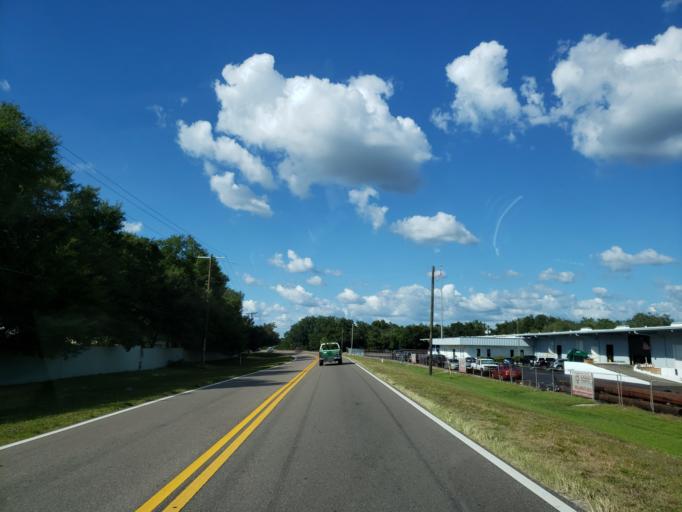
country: US
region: Florida
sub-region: Hillsborough County
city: Dover
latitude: 28.0087
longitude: -82.1706
